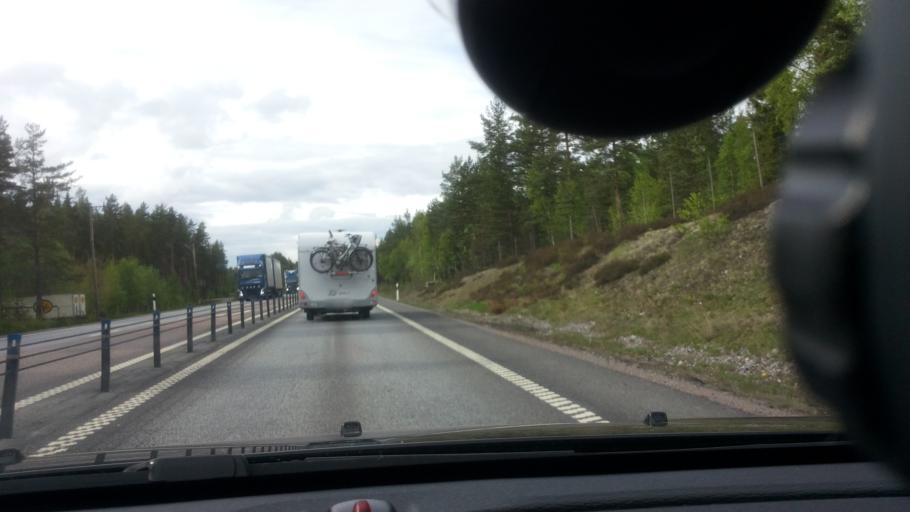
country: SE
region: Gaevleborg
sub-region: Gavle Kommun
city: Norrsundet
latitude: 61.0126
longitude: 16.9813
